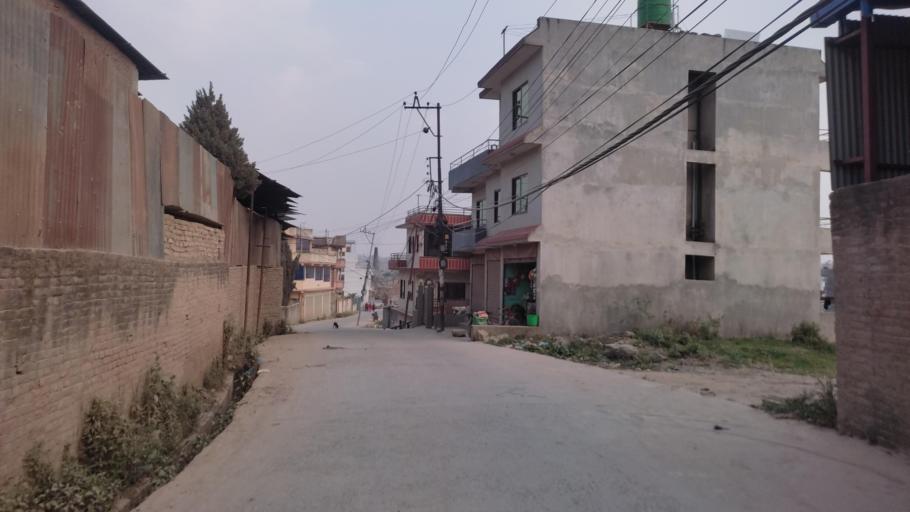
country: NP
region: Central Region
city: Kirtipur
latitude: 27.6829
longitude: 85.2565
